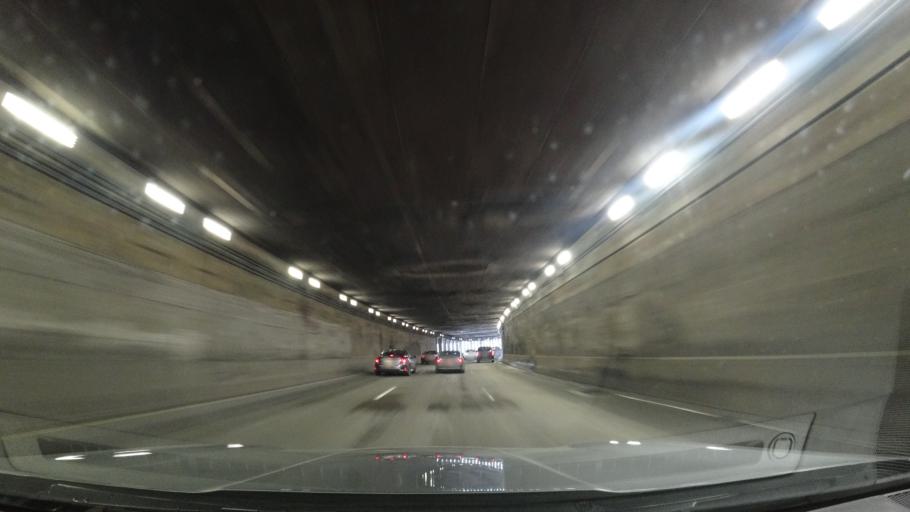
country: US
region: New York
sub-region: New York County
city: Manhattan
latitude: 40.7764
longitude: -73.9425
